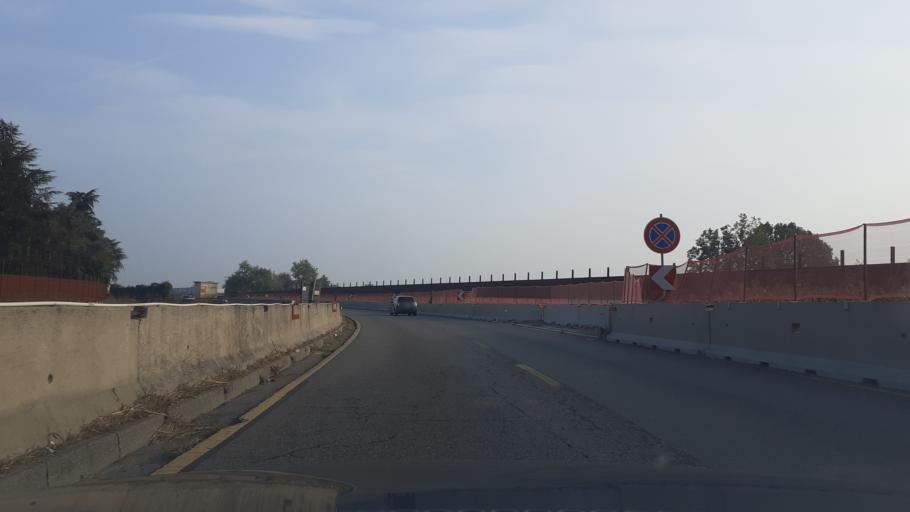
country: IT
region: Lombardy
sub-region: Citta metropolitana di Milano
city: Novate Milanese
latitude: 45.5452
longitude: 9.1479
